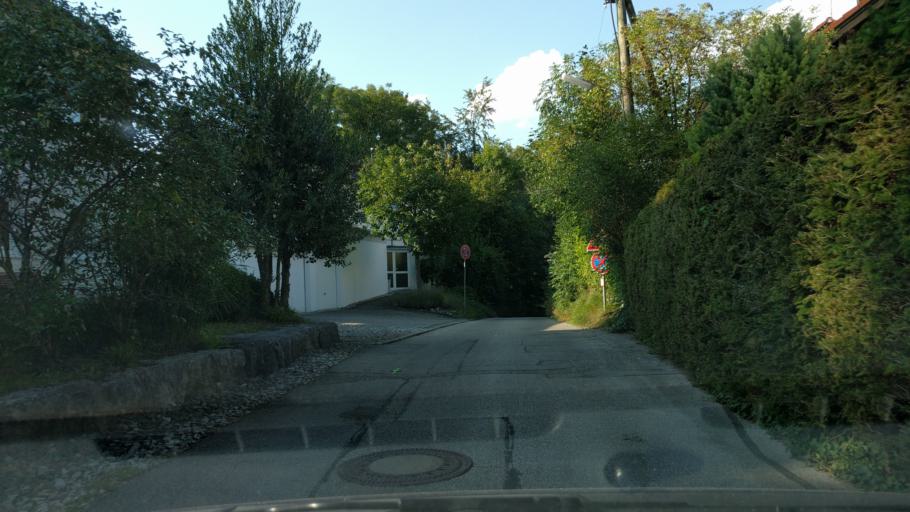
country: DE
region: Bavaria
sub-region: Upper Bavaria
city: Grunwald
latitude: 48.0366
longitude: 11.5198
